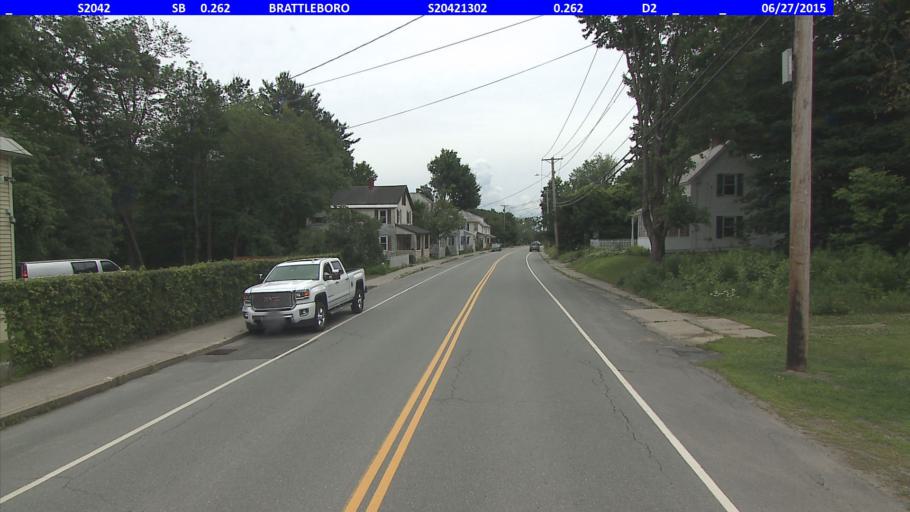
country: US
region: Vermont
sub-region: Windham County
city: Brattleboro
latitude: 42.8411
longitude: -72.5559
